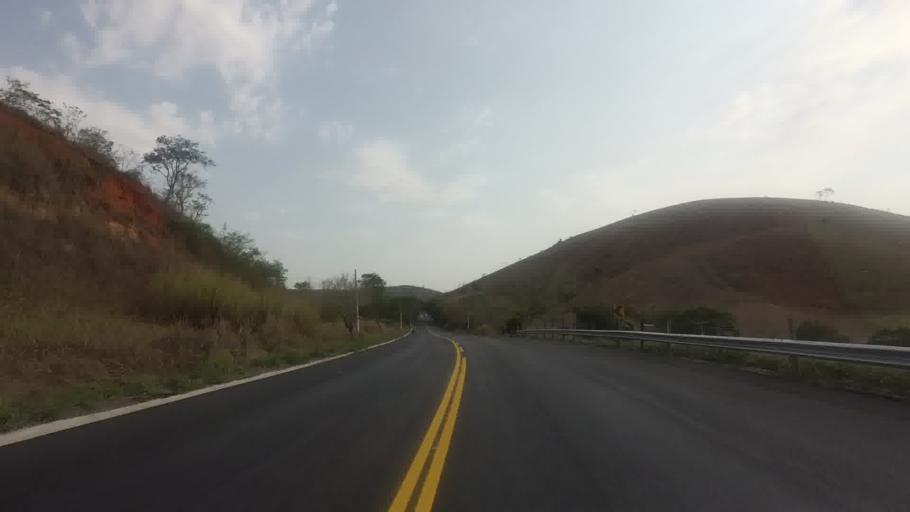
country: BR
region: Rio de Janeiro
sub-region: Bom Jesus Do Itabapoana
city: Bom Jesus do Itabapoana
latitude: -21.2423
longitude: -41.7556
